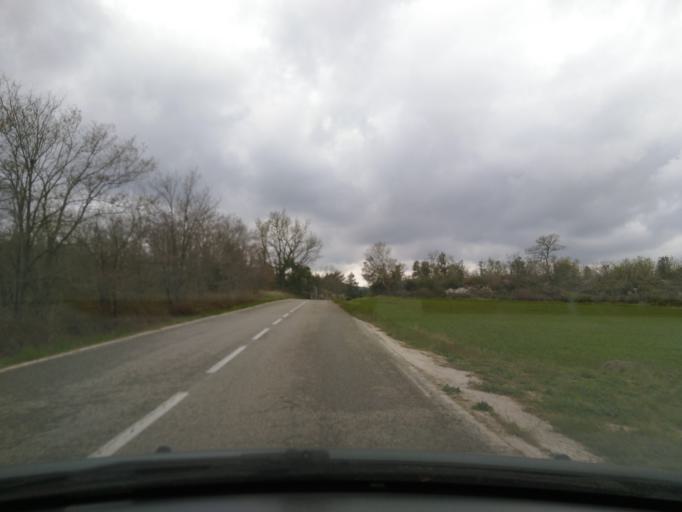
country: FR
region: Languedoc-Roussillon
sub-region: Departement du Gard
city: Barjac
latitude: 44.3583
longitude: 4.3747
